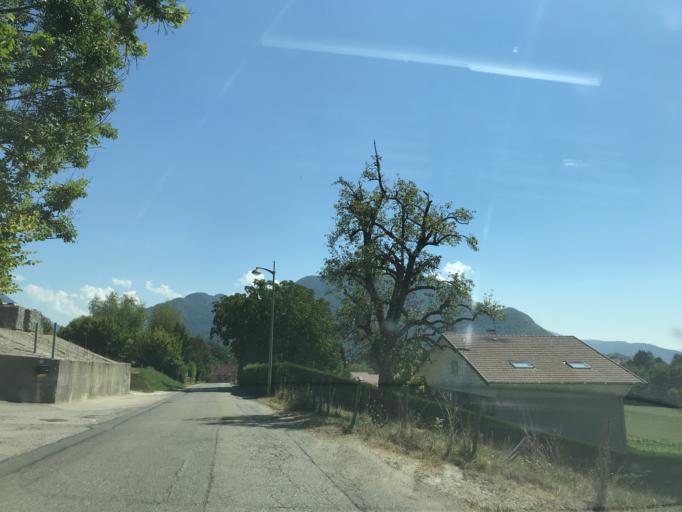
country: FR
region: Rhone-Alpes
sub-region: Departement de la Haute-Savoie
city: Villaz
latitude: 45.9397
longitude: 6.1930
